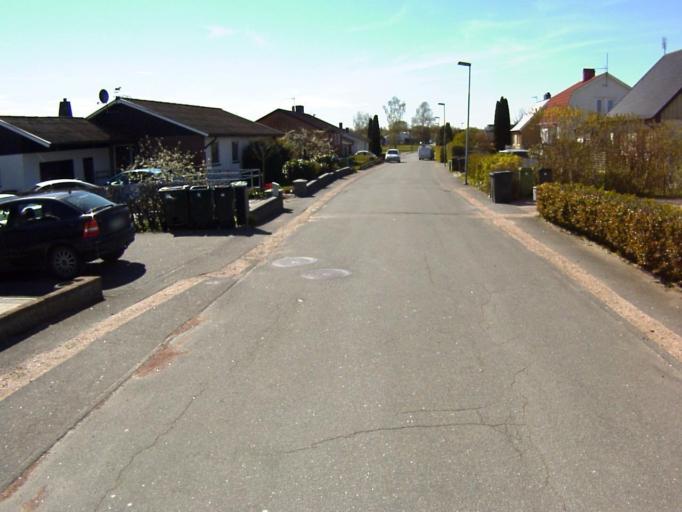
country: SE
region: Skane
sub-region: Kristianstads Kommun
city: Kristianstad
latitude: 56.0111
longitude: 14.1512
